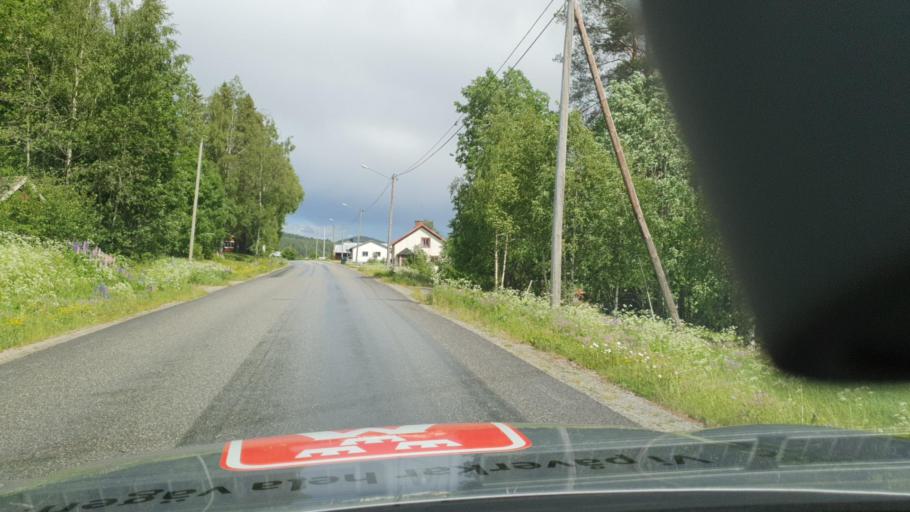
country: SE
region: Vaesternorrland
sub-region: OErnskoeldsviks Kommun
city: Bredbyn
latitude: 63.3319
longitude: 18.1395
